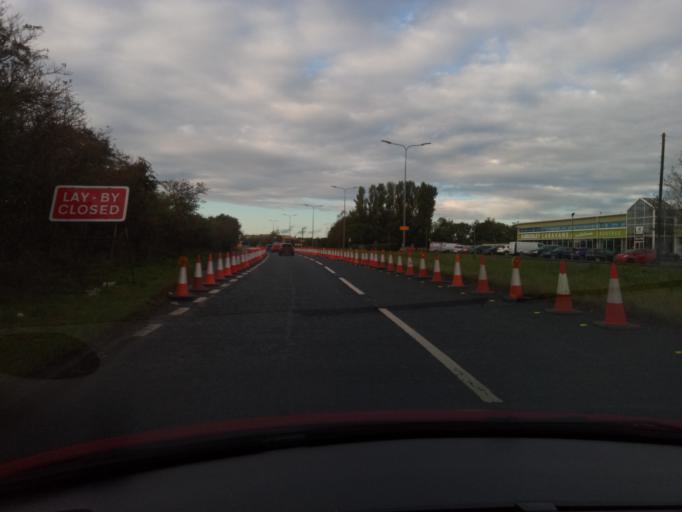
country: GB
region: England
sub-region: Darlington
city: Heighington
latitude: 54.5620
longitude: -1.5971
